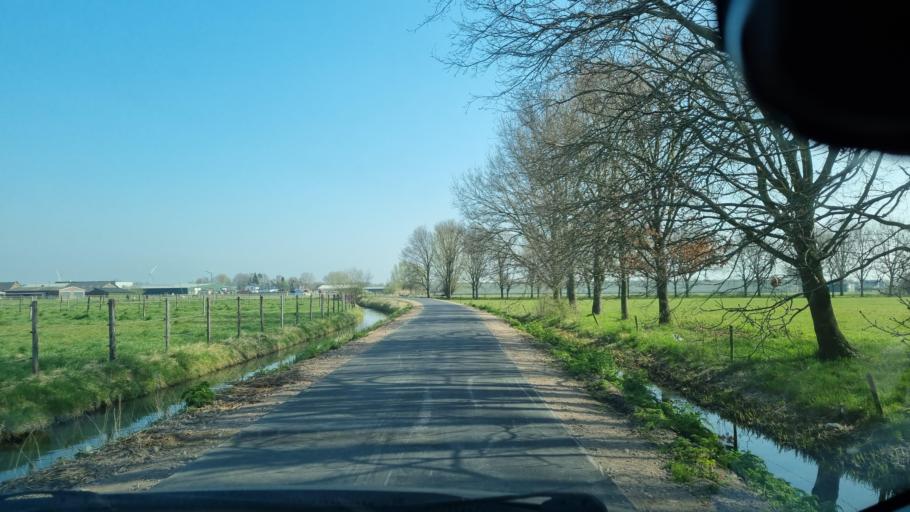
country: NL
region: Gelderland
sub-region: Gemeente Maasdriel
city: Hedel
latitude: 51.7446
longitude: 5.2341
